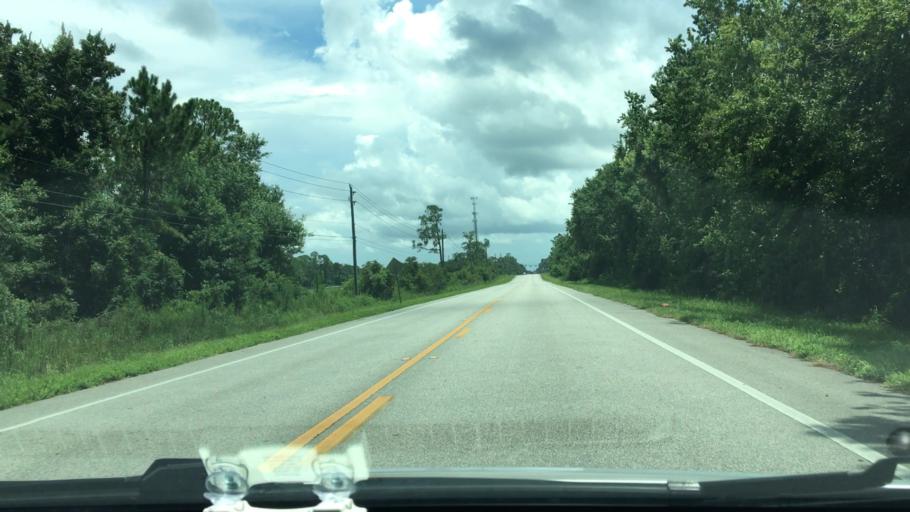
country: US
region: Florida
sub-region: Volusia County
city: Samsula-Spruce Creek
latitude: 29.0171
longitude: -81.0680
